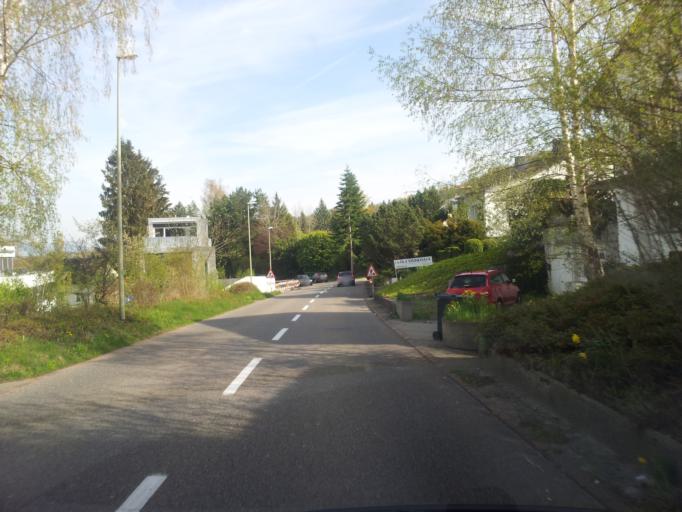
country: CH
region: Zurich
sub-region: Bezirk Uster
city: Gockhausen
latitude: 47.3828
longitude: 8.5930
